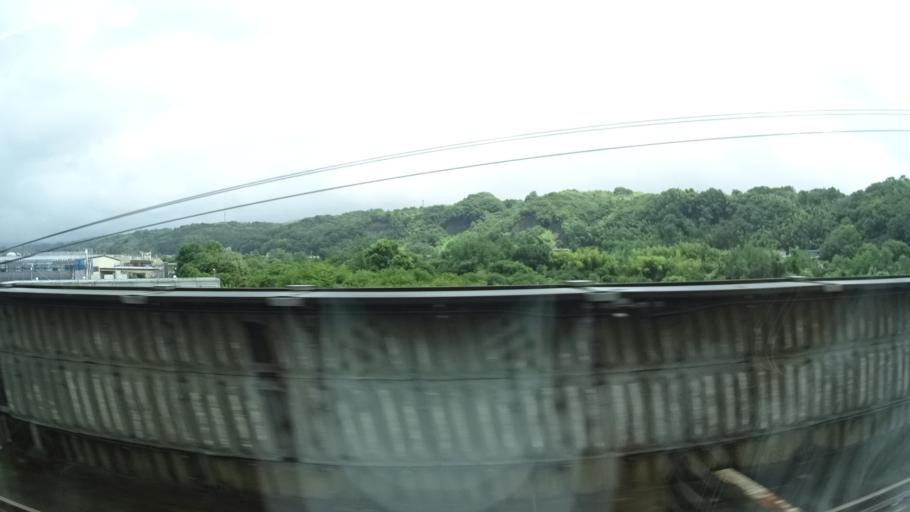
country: JP
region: Gunma
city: Annaka
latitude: 36.3705
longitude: 138.8988
